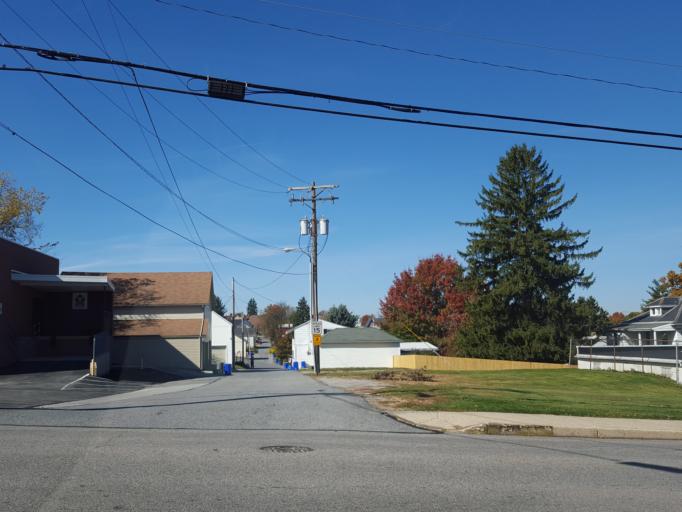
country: US
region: Pennsylvania
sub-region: York County
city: Dallastown
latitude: 39.9015
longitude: -76.6440
